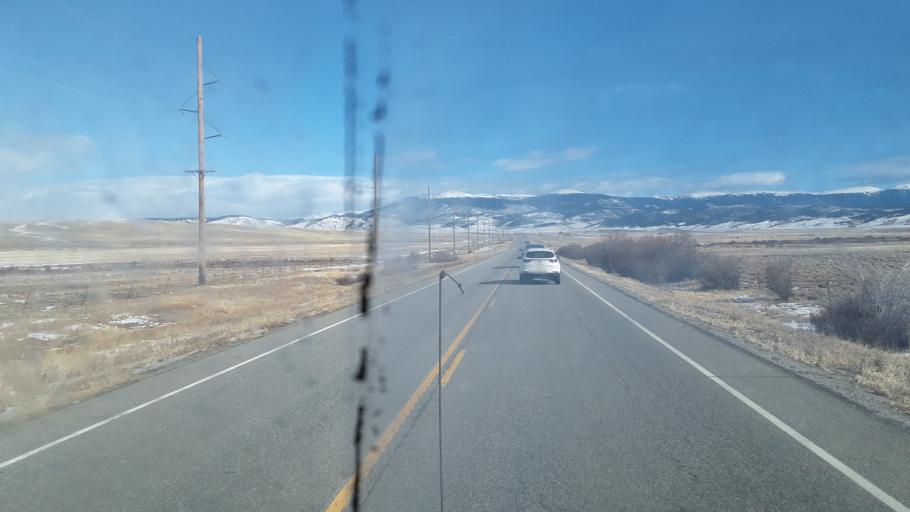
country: US
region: Colorado
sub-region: Park County
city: Fairplay
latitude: 39.3492
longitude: -105.8347
